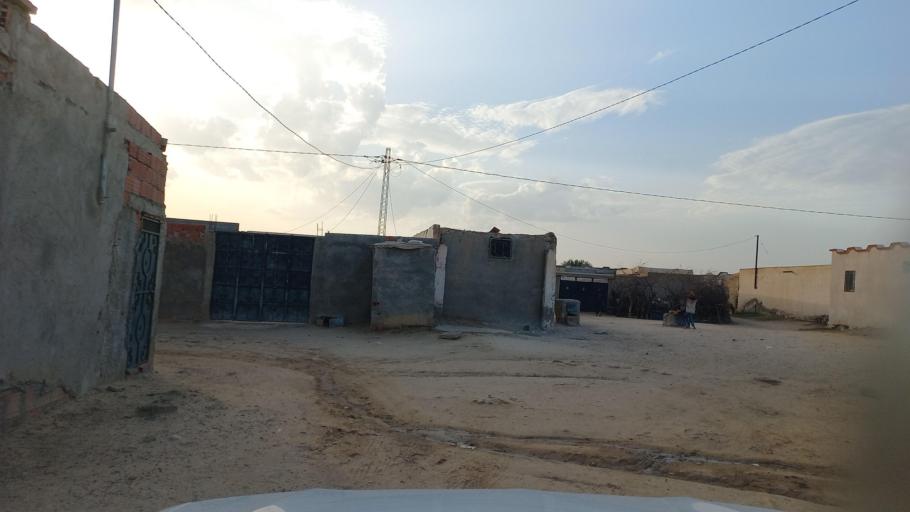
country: TN
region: Al Qasrayn
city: Kasserine
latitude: 35.2710
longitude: 9.0679
